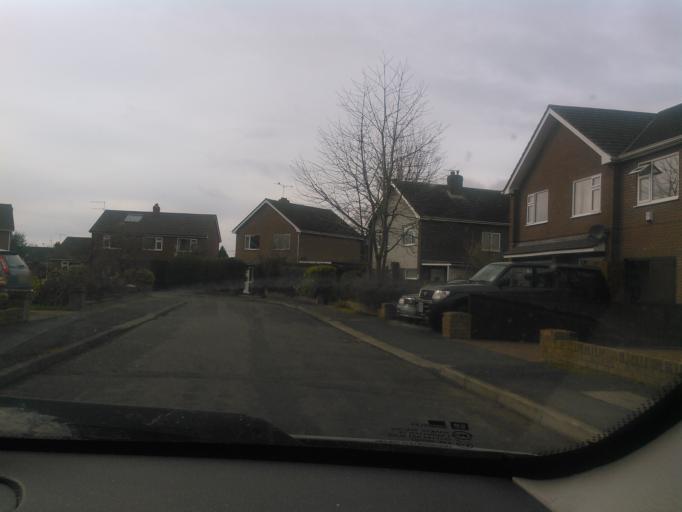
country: GB
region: England
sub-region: Shropshire
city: Wem
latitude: 52.8621
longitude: -2.7243
